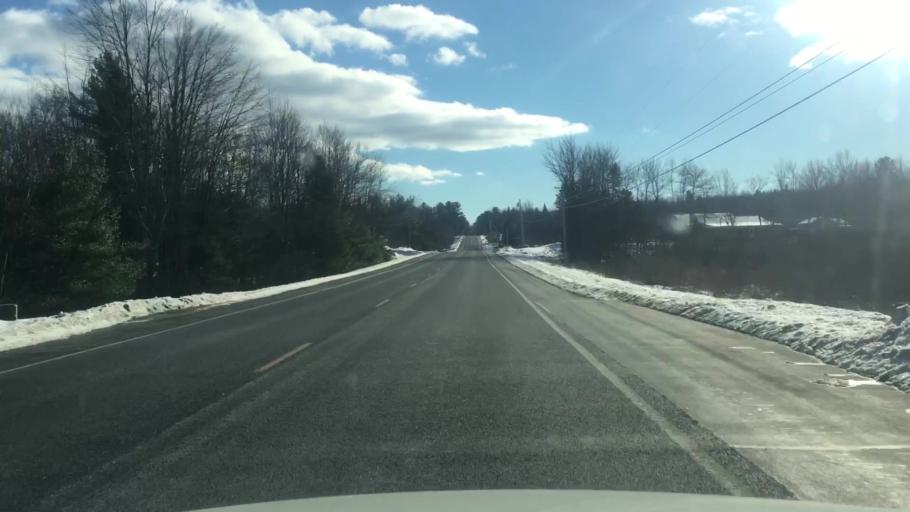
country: US
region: Maine
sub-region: Somerset County
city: Madison
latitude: 44.8454
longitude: -69.7894
